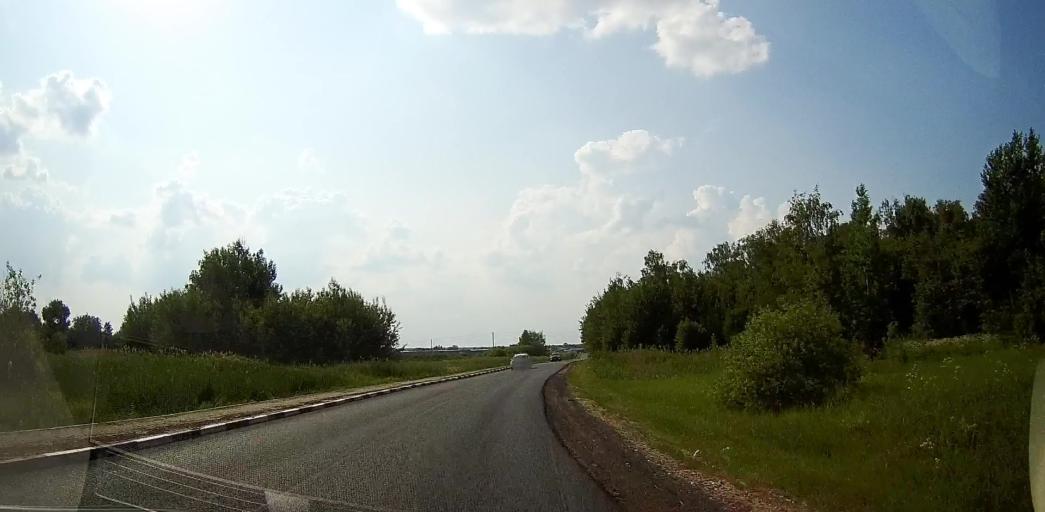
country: RU
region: Moskovskaya
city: Il'inskoye
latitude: 55.2203
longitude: 37.9358
